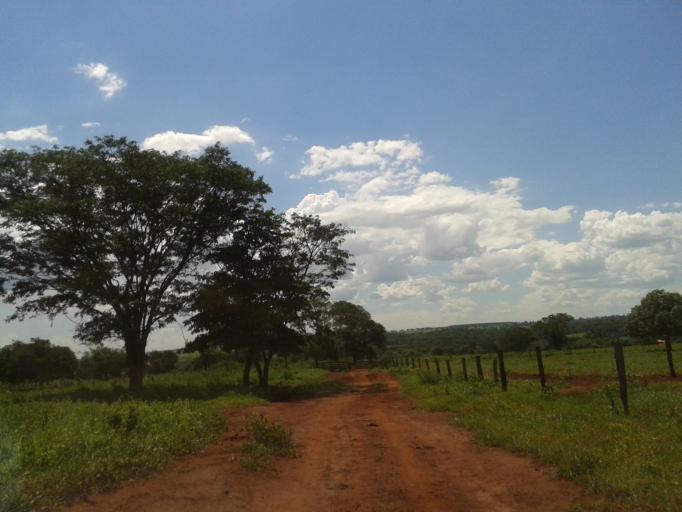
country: BR
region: Minas Gerais
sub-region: Santa Vitoria
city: Santa Vitoria
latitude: -19.1040
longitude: -50.5234
